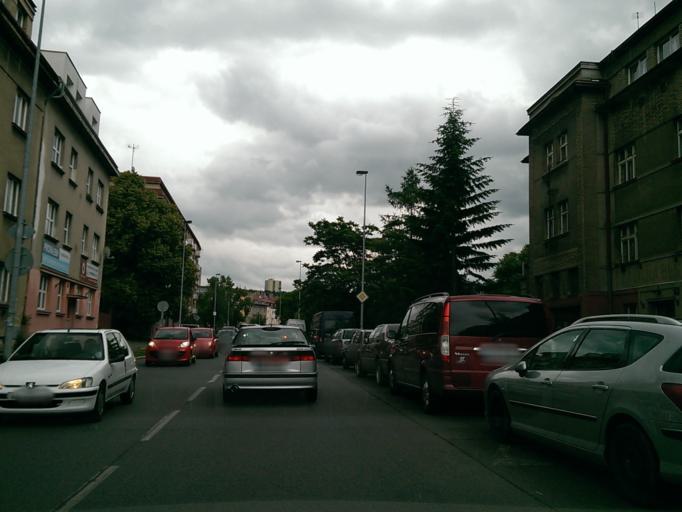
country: CZ
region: Praha
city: Branik
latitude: 50.0355
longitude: 14.4124
